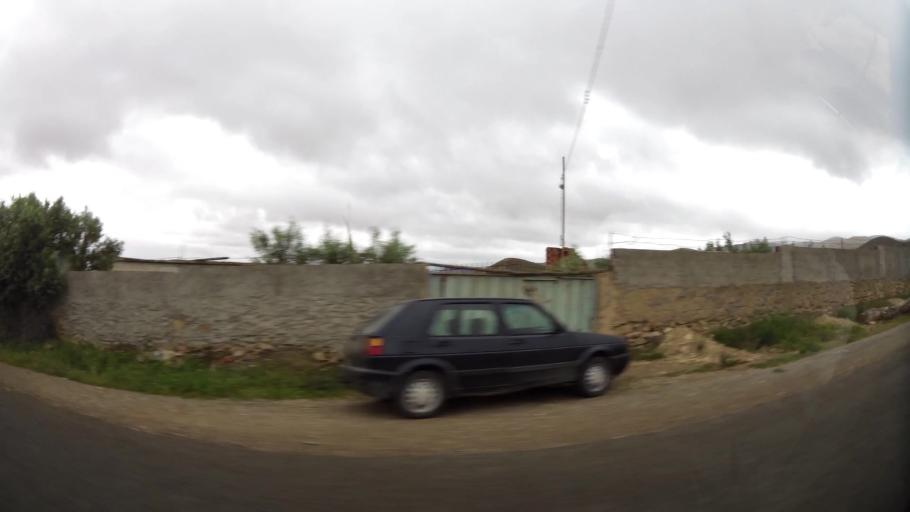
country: MA
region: Oriental
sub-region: Nador
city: Midar
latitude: 35.0638
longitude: -3.4699
